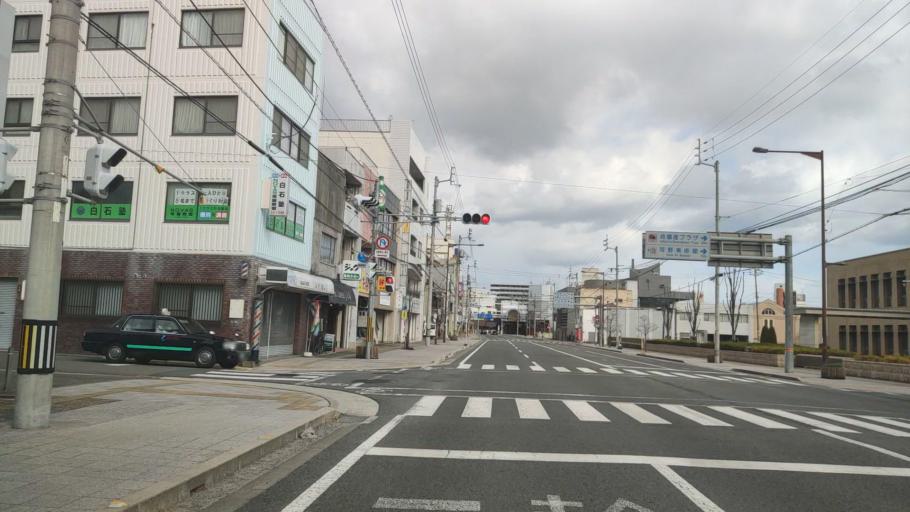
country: JP
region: Ehime
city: Hojo
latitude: 34.0637
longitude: 132.9972
